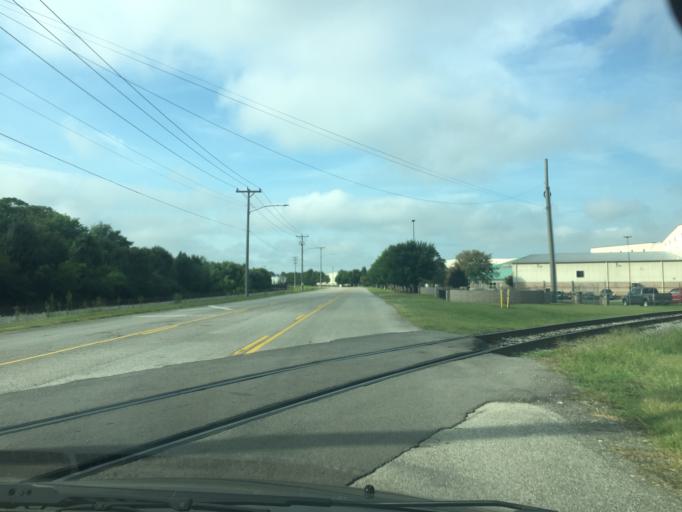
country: US
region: Tennessee
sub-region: Hamilton County
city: East Chattanooga
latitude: 35.0790
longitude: -85.2713
